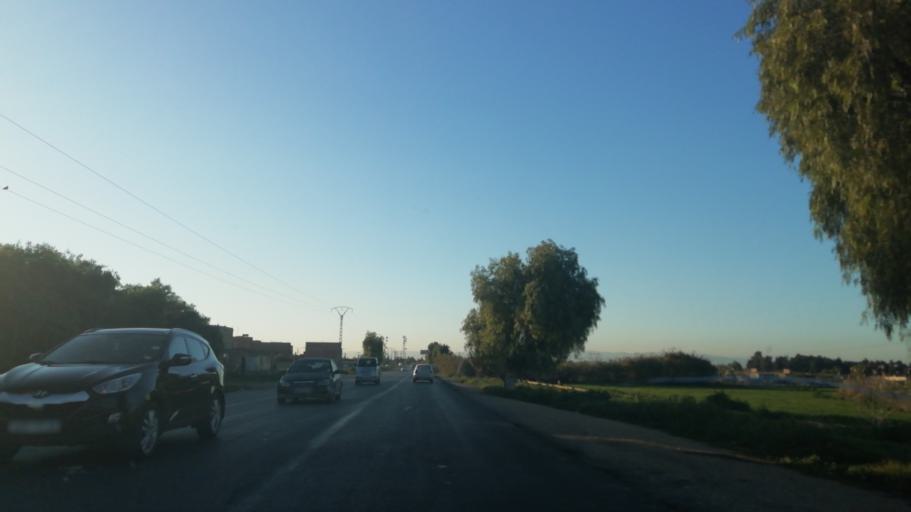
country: DZ
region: Relizane
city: Relizane
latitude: 35.7645
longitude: 0.6431
